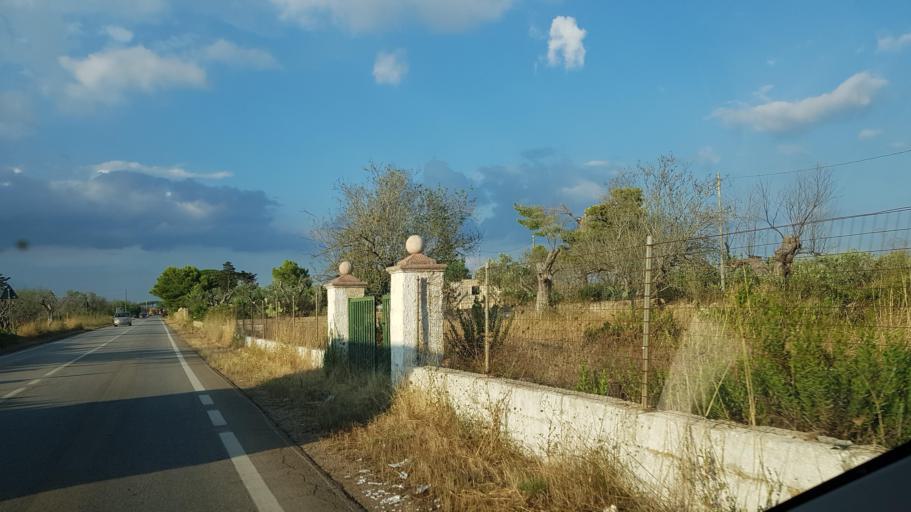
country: IT
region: Apulia
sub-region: Provincia di Lecce
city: Acquarica del Capo
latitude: 39.8766
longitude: 18.2267
